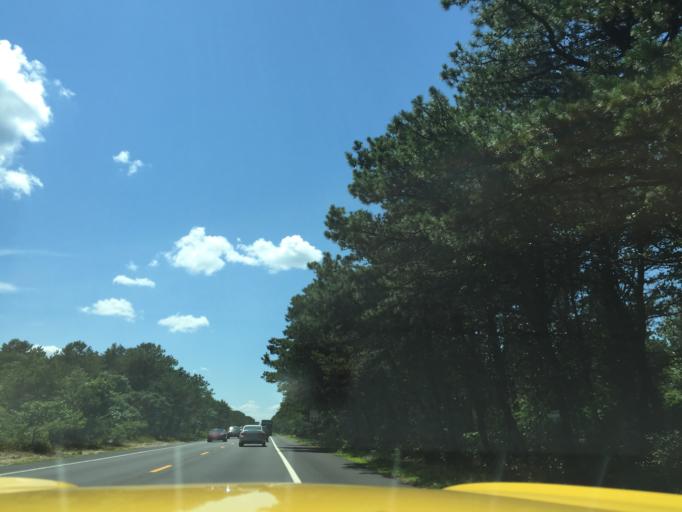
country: US
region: New York
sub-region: Suffolk County
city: Amagansett
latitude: 40.9918
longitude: -72.0691
